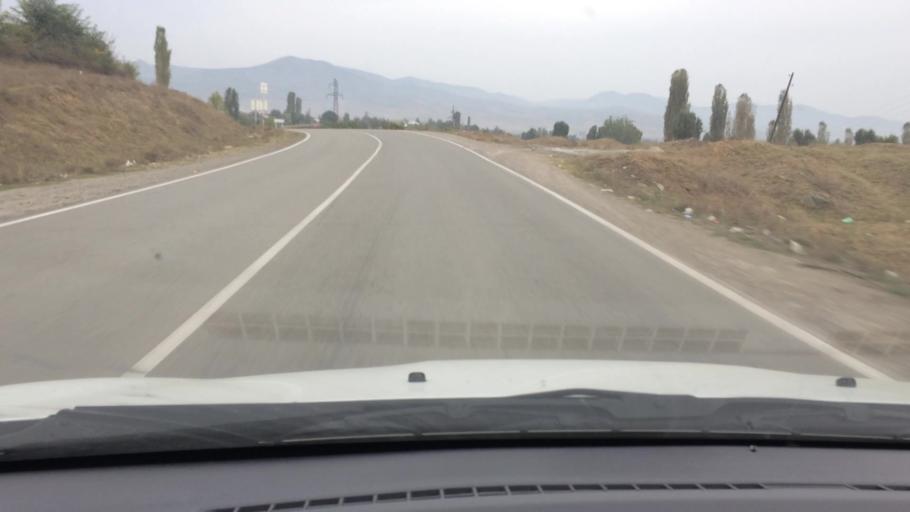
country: AM
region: Tavush
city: Bagratashen
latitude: 41.2330
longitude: 44.8156
